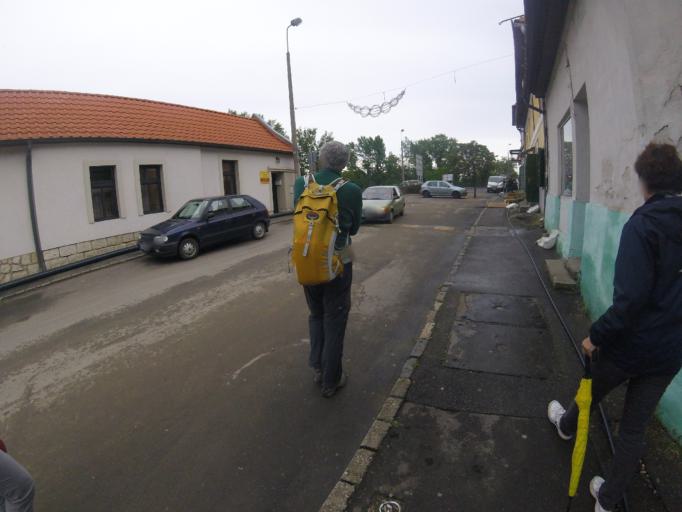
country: HU
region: Borsod-Abauj-Zemplen
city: Tokaj
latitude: 48.1222
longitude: 21.4120
